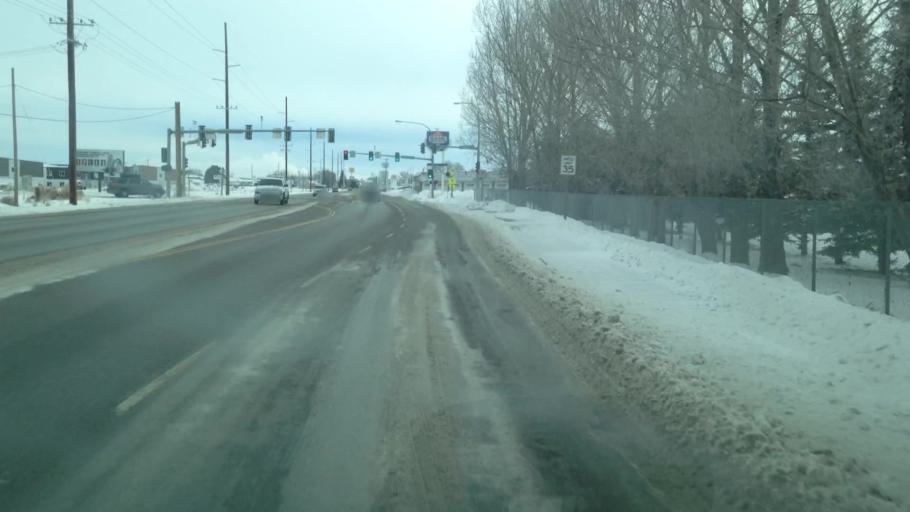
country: US
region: Idaho
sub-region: Madison County
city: Rexburg
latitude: 43.8108
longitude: -111.8031
